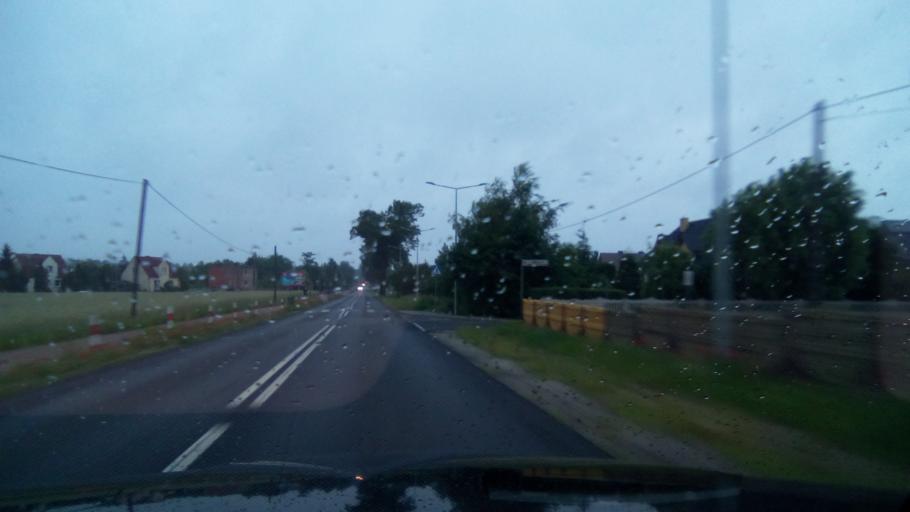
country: PL
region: Greater Poland Voivodeship
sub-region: Powiat poznanski
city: Kobylnica
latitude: 52.4379
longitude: 17.0743
